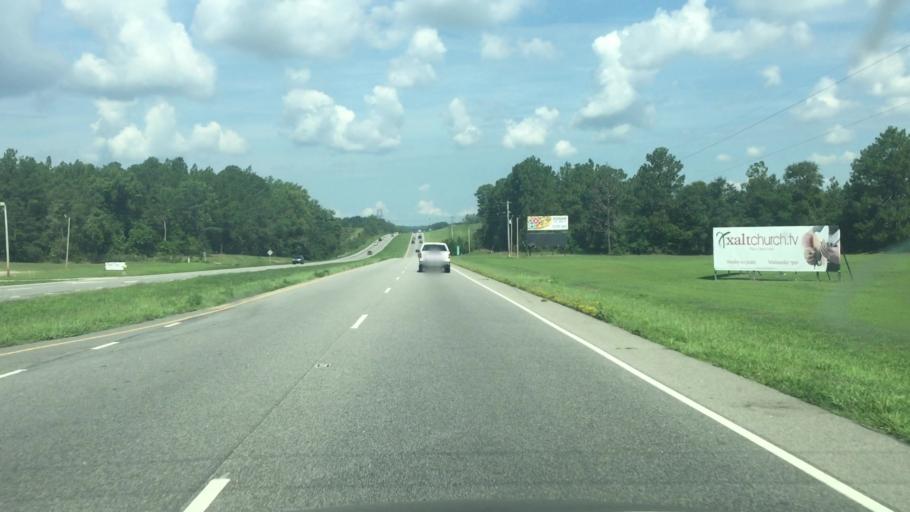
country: US
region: North Carolina
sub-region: Scotland County
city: Laurel Hill
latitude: 34.8446
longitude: -79.6086
